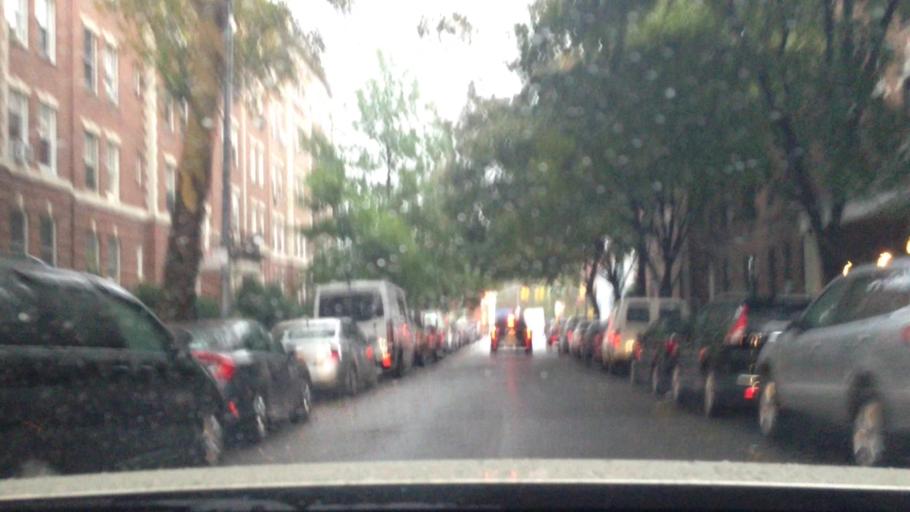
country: US
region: New York
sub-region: Queens County
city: Long Island City
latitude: 40.7502
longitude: -73.8901
